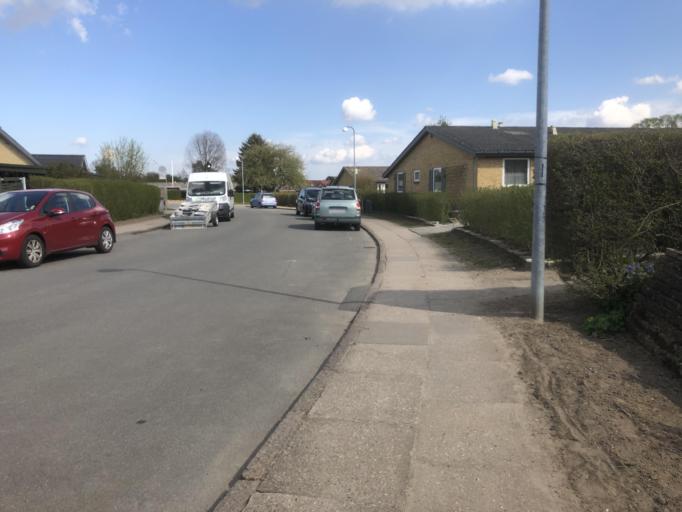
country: DK
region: South Denmark
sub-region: Odense Kommune
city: Odense
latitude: 55.4059
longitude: 10.3325
